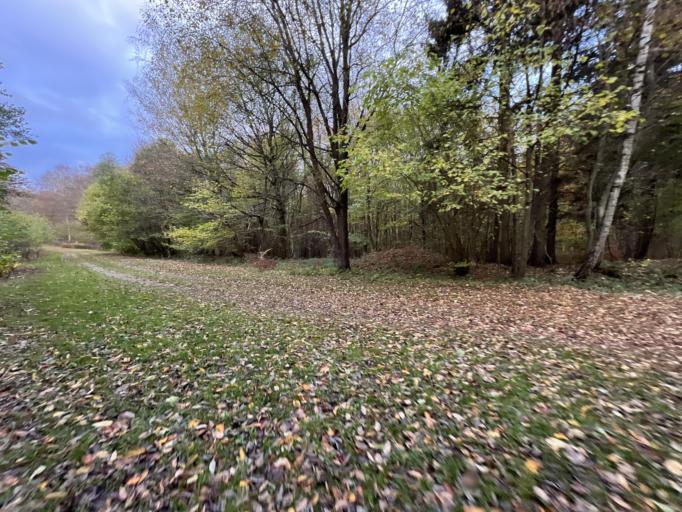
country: DE
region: Mecklenburg-Vorpommern
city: Putbus
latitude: 54.3736
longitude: 13.4675
